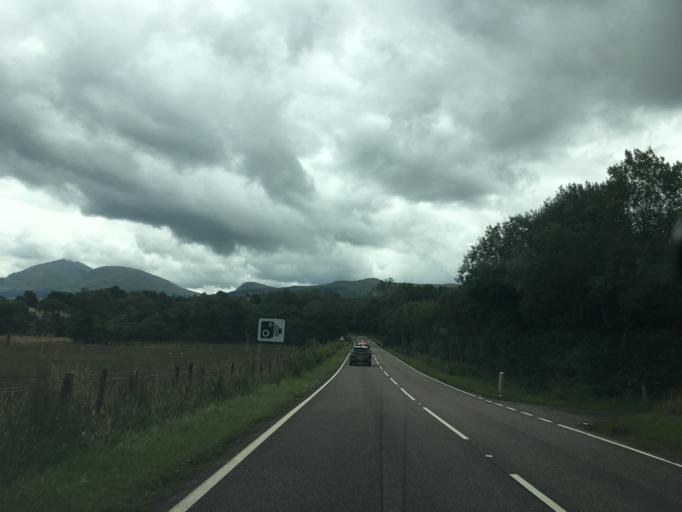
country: GB
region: Scotland
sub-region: Argyll and Bute
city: Garelochhead
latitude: 56.4030
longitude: -4.9959
